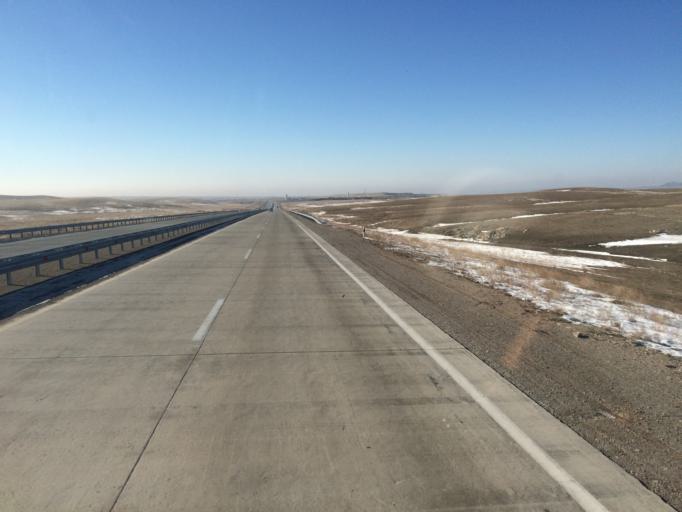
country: KZ
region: Zhambyl
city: Georgiyevka
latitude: 43.3568
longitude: 74.5895
